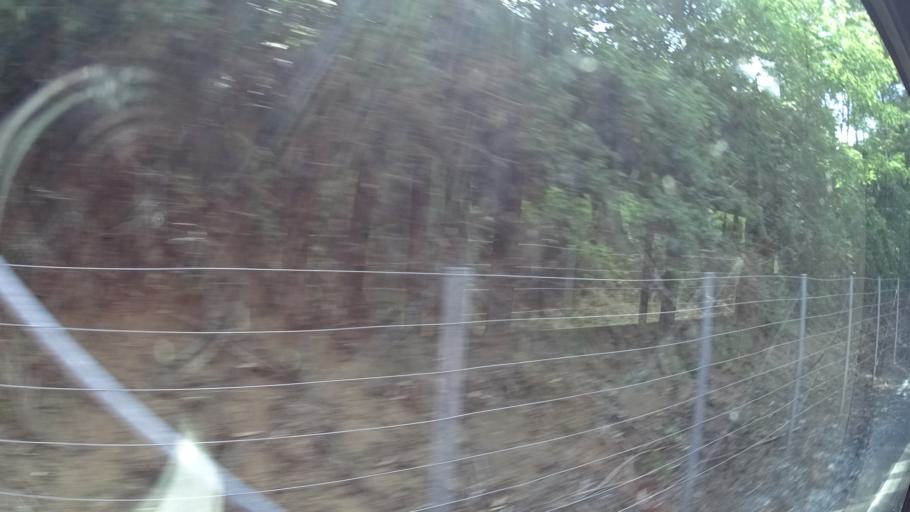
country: JP
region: Iwate
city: Ofunato
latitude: 39.0205
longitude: 141.7134
